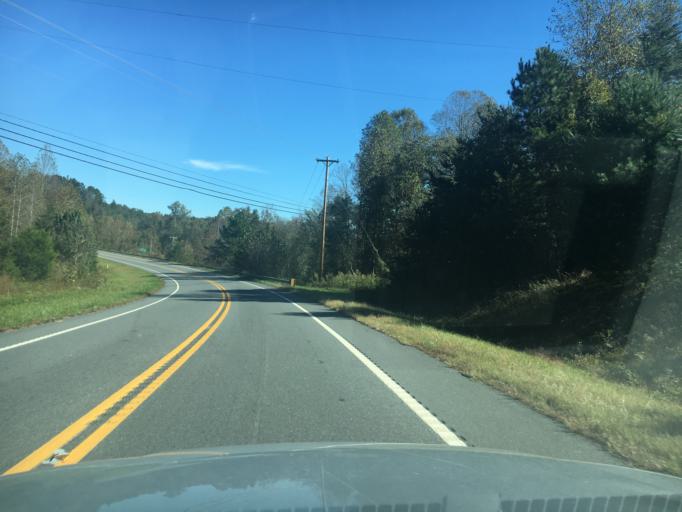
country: US
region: North Carolina
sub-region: Rutherford County
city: Spindale
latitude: 35.3949
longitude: -81.9285
